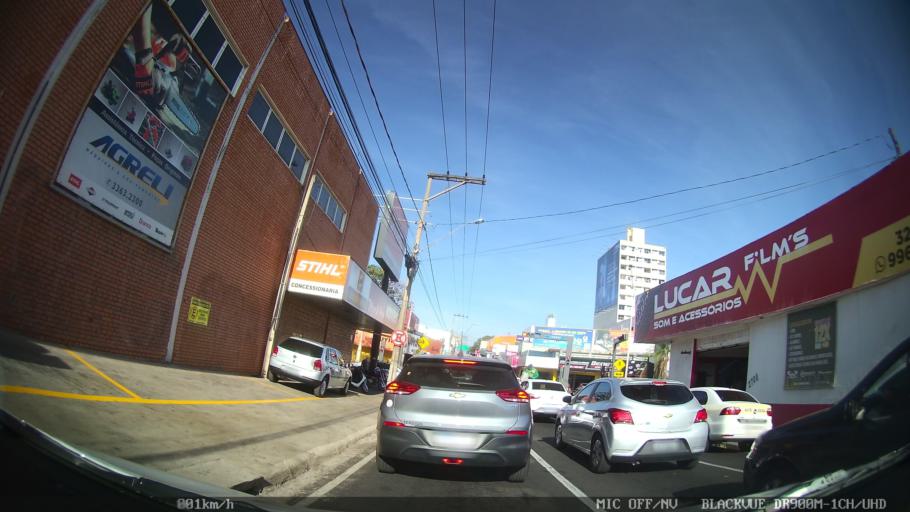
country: BR
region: Sao Paulo
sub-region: Sao Jose Do Rio Preto
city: Sao Jose do Rio Preto
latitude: -20.8075
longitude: -49.3807
